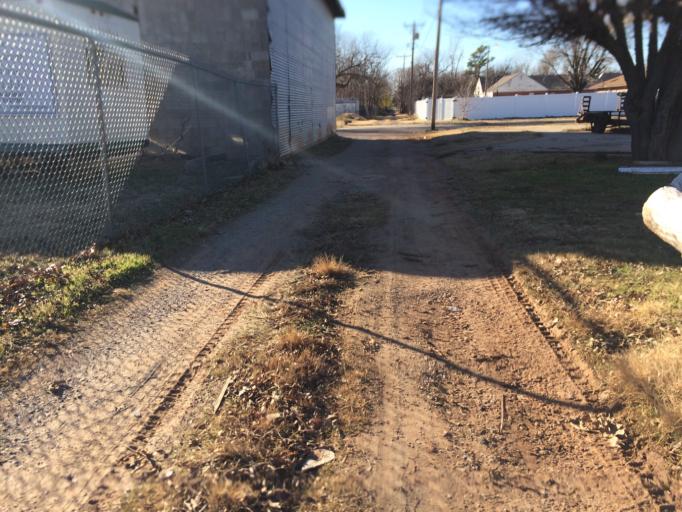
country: US
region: Oklahoma
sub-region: Cleveland County
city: Norman
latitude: 35.2319
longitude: -97.4422
